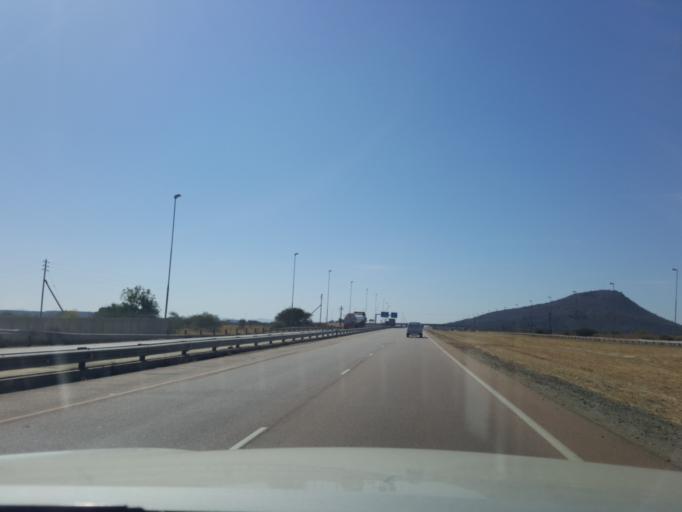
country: ZA
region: North-West
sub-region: Bojanala Platinum District Municipality
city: Brits
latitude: -25.7231
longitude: 27.6778
